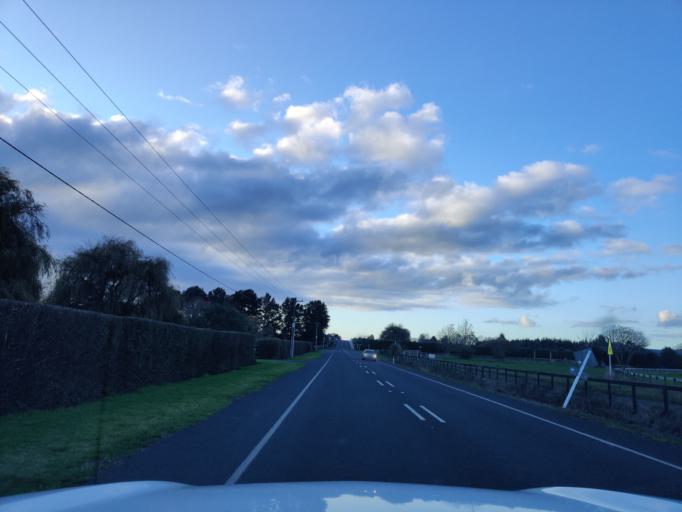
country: NZ
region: Waikato
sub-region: Waipa District
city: Cambridge
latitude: -37.8732
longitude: 175.4389
